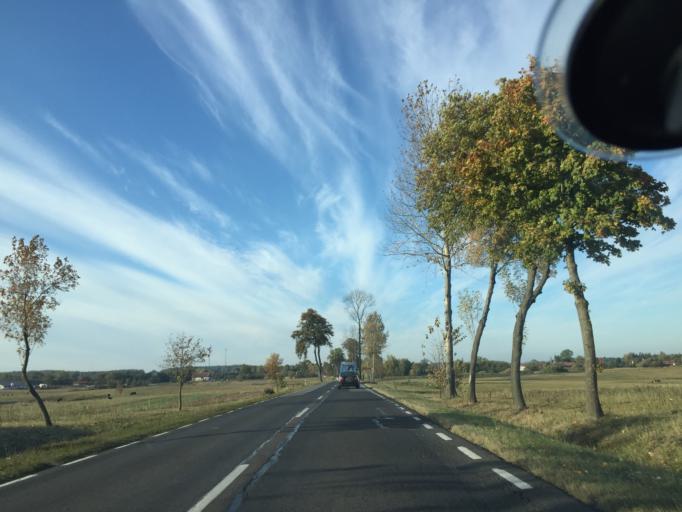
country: PL
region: Warmian-Masurian Voivodeship
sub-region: Powiat bartoszycki
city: Bartoszyce
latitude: 54.1917
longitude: 20.7280
